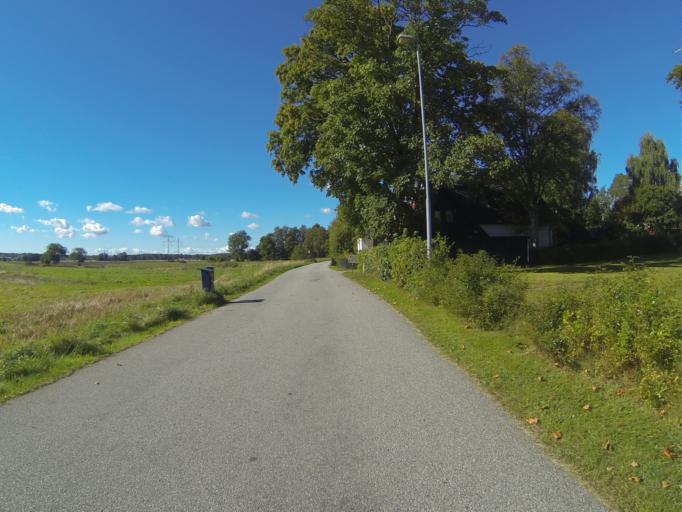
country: SE
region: Skane
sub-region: Hoors Kommun
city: Loberod
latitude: 55.7263
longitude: 13.3928
